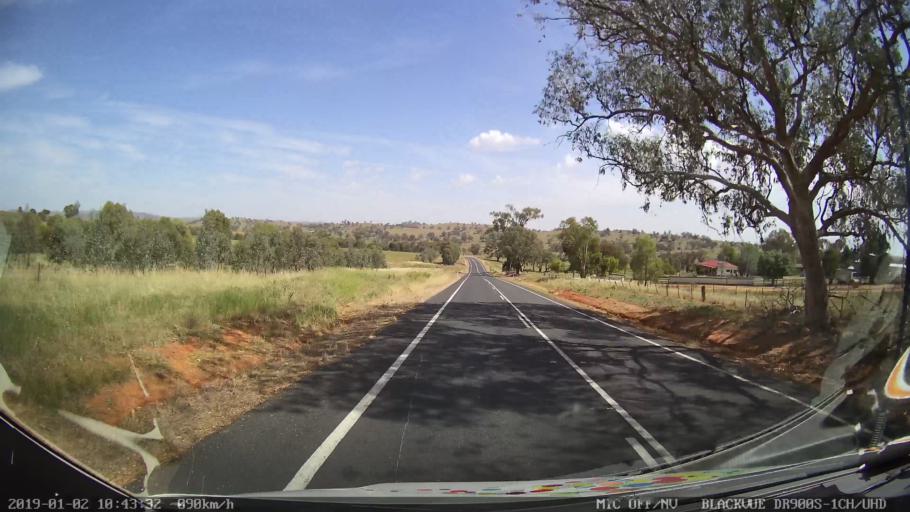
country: AU
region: New South Wales
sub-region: Cootamundra
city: Cootamundra
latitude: -34.7713
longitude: 148.3035
